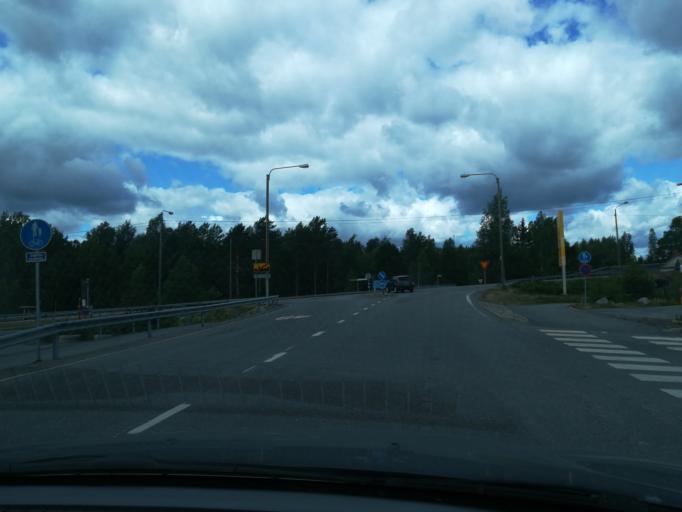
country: FI
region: Southern Savonia
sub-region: Mikkeli
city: Ristiina
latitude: 61.5131
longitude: 27.2427
